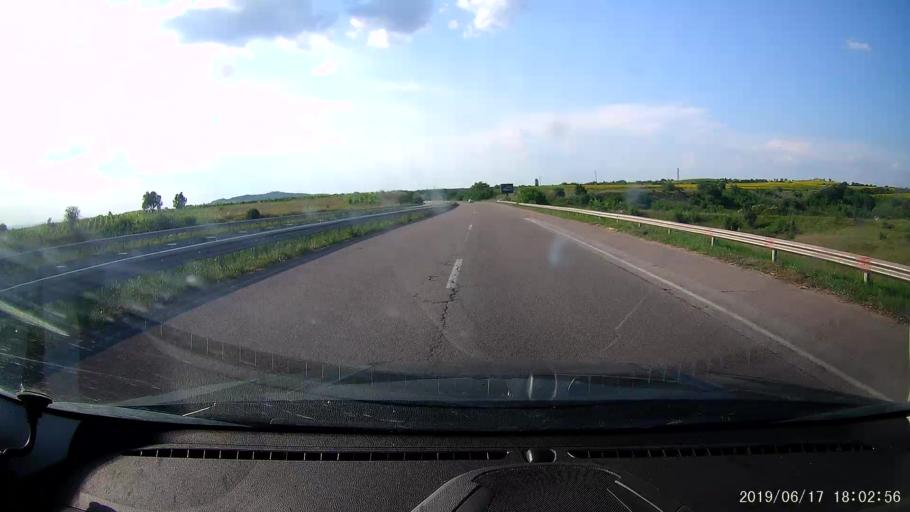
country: BG
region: Khaskovo
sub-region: Obshtina Svilengrad
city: Svilengrad
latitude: 41.7690
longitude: 26.2256
